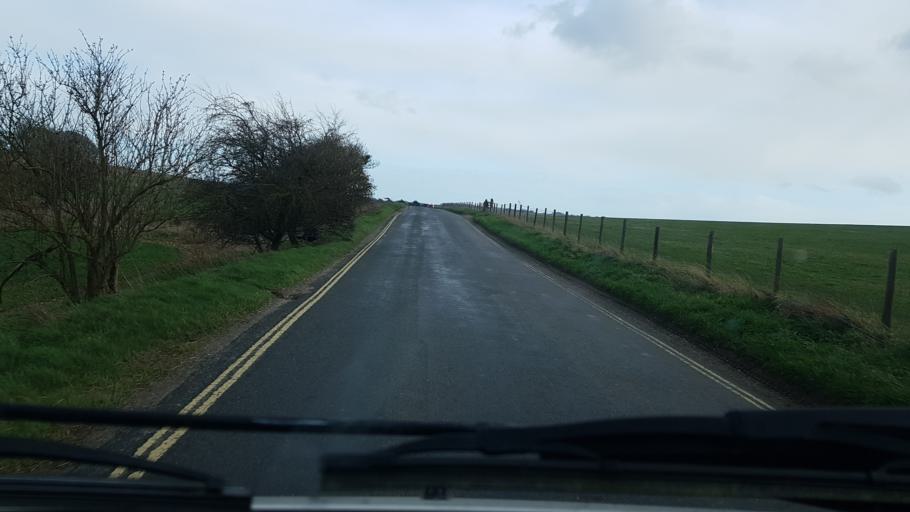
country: GB
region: England
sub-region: Wiltshire
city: Avebury
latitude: 51.4200
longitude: -1.8447
